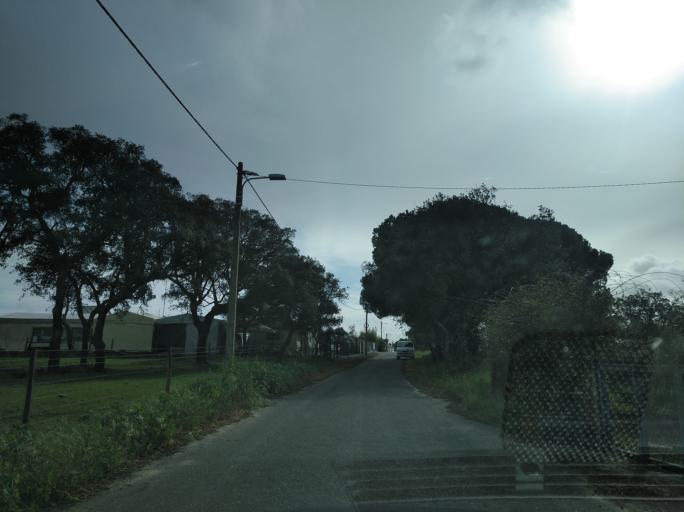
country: PT
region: Setubal
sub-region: Grandola
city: Grandola
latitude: 38.2005
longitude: -8.5456
